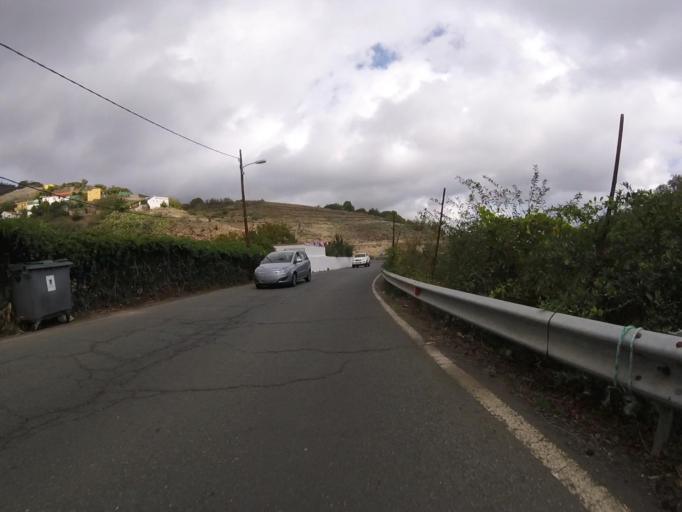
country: ES
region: Canary Islands
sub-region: Provincia de Las Palmas
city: Vega de San Mateo
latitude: 27.9936
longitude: -15.5675
